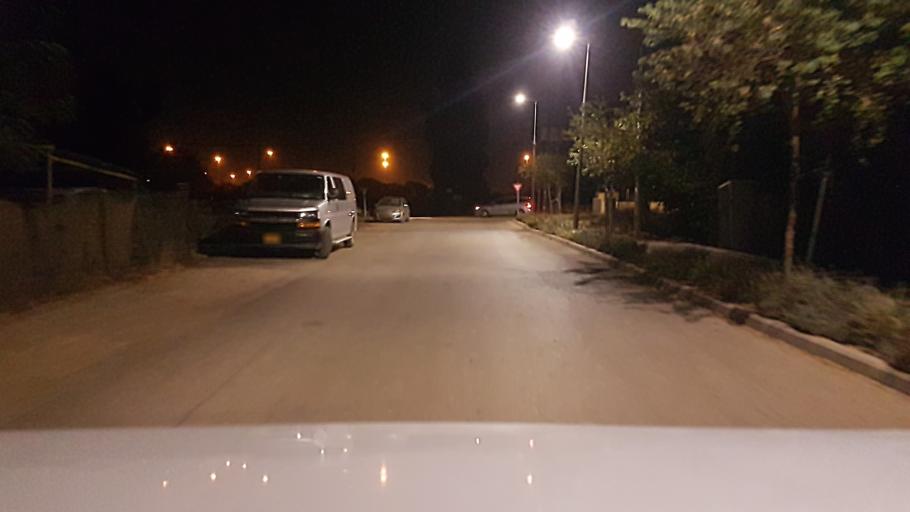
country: IL
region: Central District
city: Nehalim
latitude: 32.0742
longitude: 34.9304
